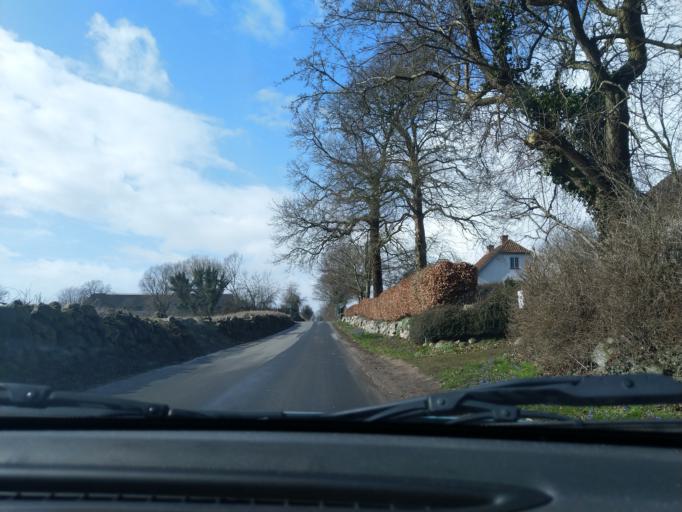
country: DK
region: Zealand
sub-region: Naestved Kommune
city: Fuglebjerg
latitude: 55.3139
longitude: 11.6700
